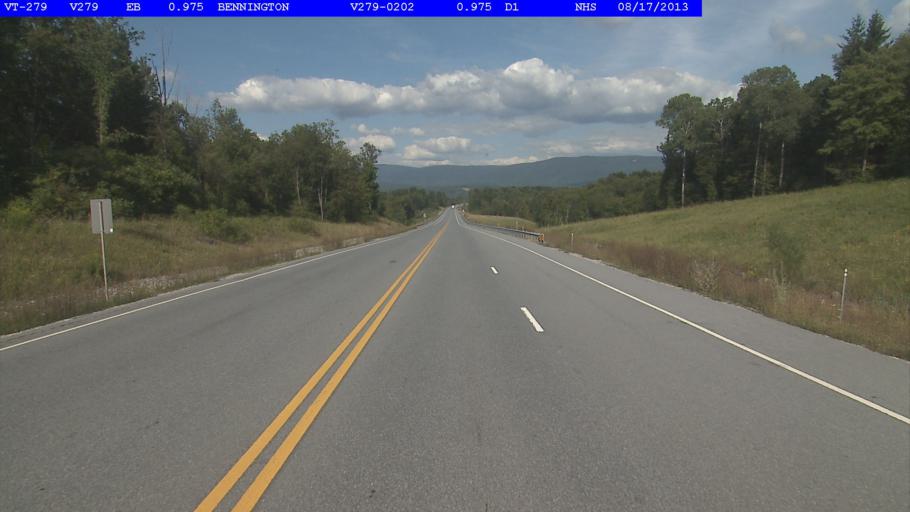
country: US
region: Vermont
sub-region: Bennington County
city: North Bennington
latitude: 42.9008
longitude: -73.2617
